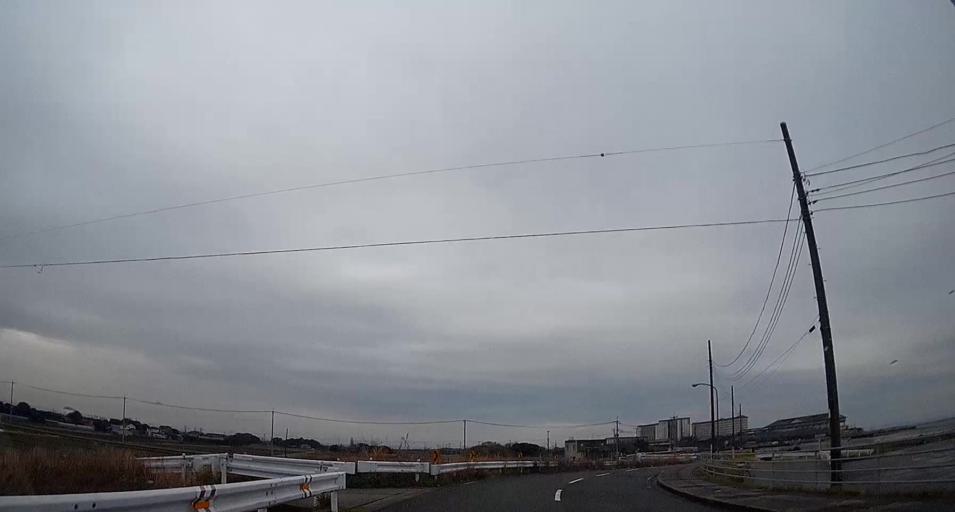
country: JP
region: Chiba
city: Kisarazu
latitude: 35.4270
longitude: 139.9027
